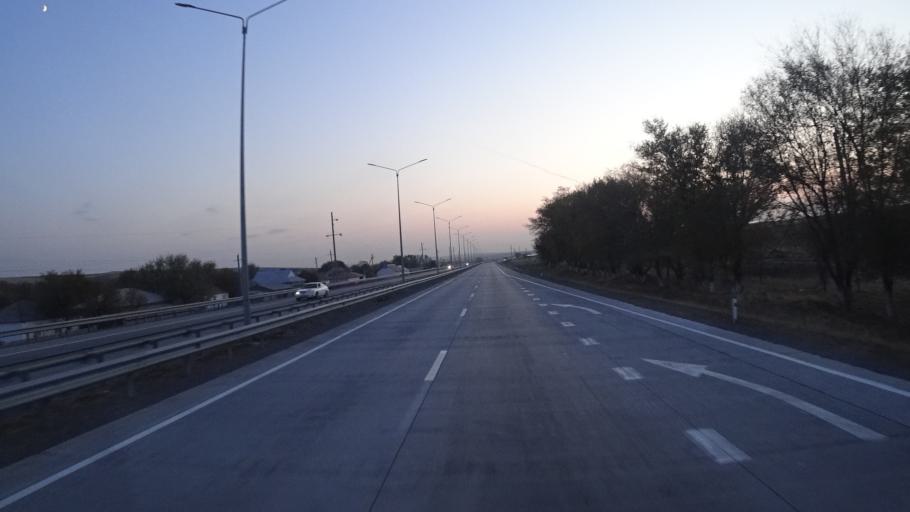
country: KZ
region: Ongtustik Qazaqstan
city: Qazyqurt
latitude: 41.8831
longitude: 69.4392
